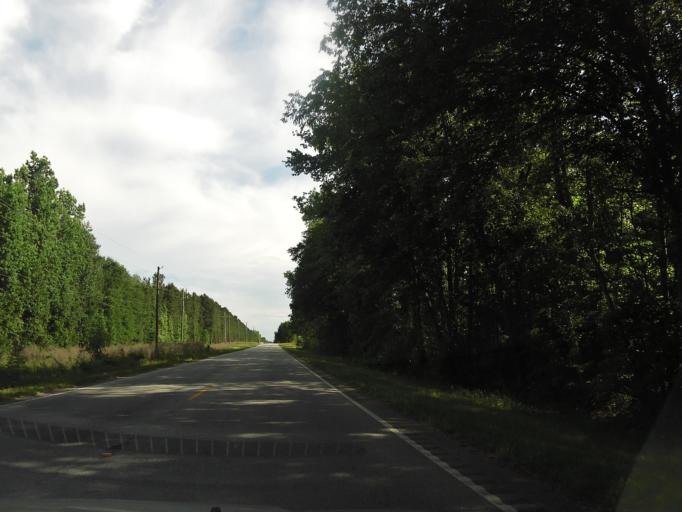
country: US
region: South Carolina
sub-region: Allendale County
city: Fairfax
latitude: 32.9338
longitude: -81.2369
